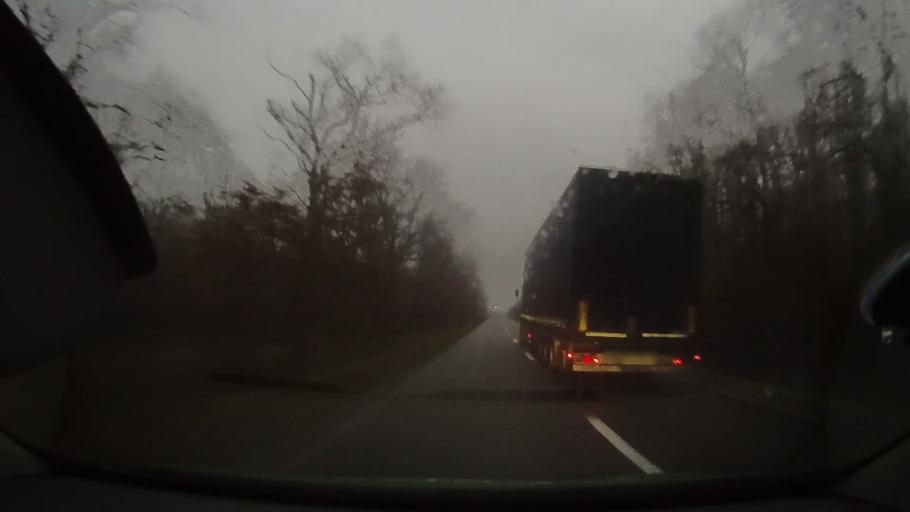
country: RO
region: Arad
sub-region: Comuna Beliu
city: Beliu
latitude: 46.5037
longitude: 21.9726
